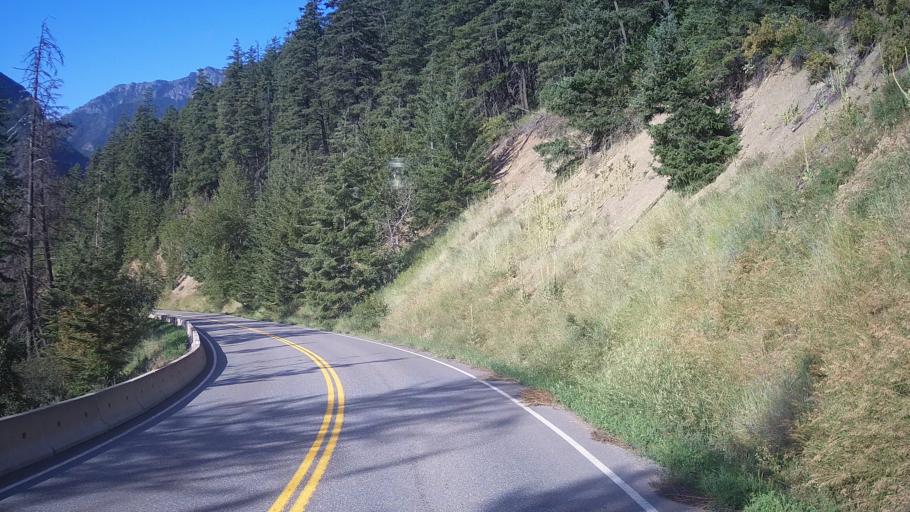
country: CA
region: British Columbia
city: Lillooet
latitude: 50.6485
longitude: -122.0212
